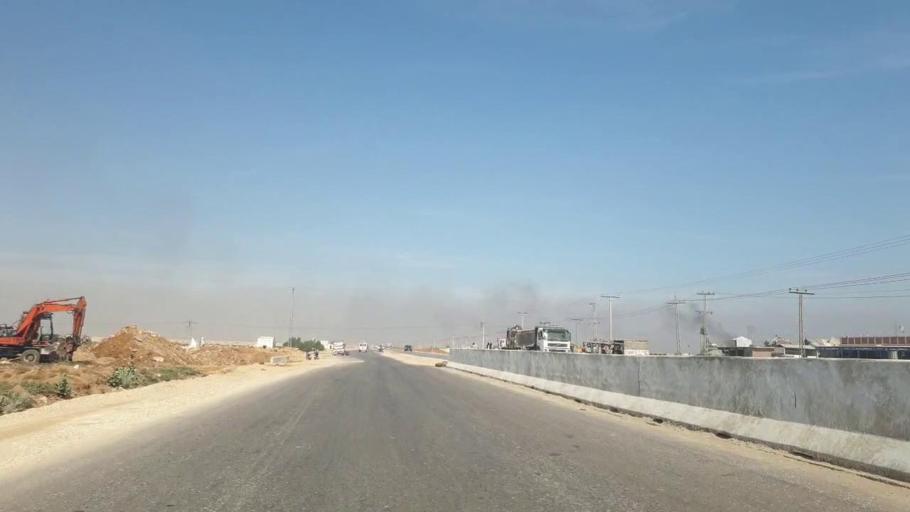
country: PK
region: Sindh
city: Jamshoro
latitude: 25.4788
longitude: 68.2720
